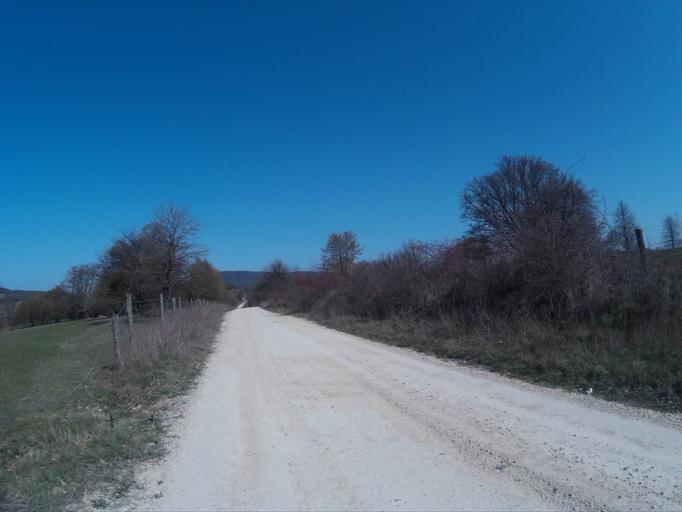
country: HU
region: Veszprem
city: Herend
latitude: 47.2100
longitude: 17.7909
